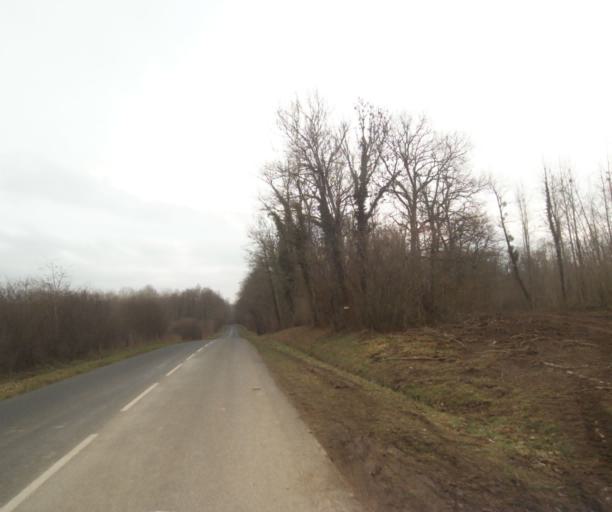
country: FR
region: Champagne-Ardenne
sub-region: Departement de la Marne
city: Pargny-sur-Saulx
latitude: 48.7401
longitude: 4.8692
